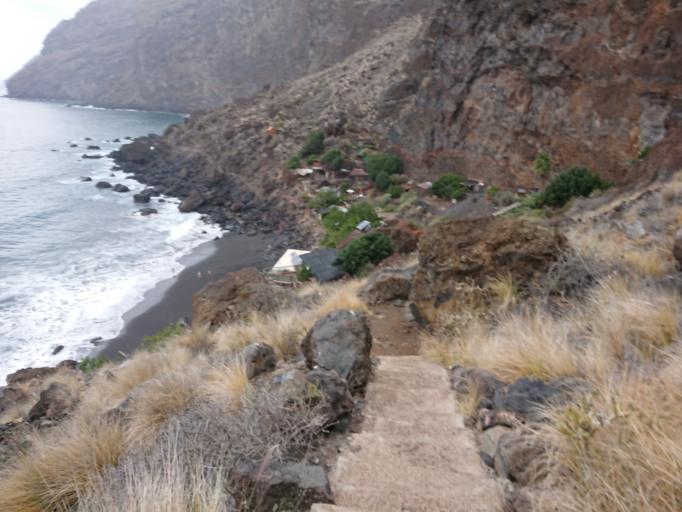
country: ES
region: Canary Islands
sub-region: Provincia de Santa Cruz de Tenerife
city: Tijarafe
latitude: 28.7209
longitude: -17.9793
